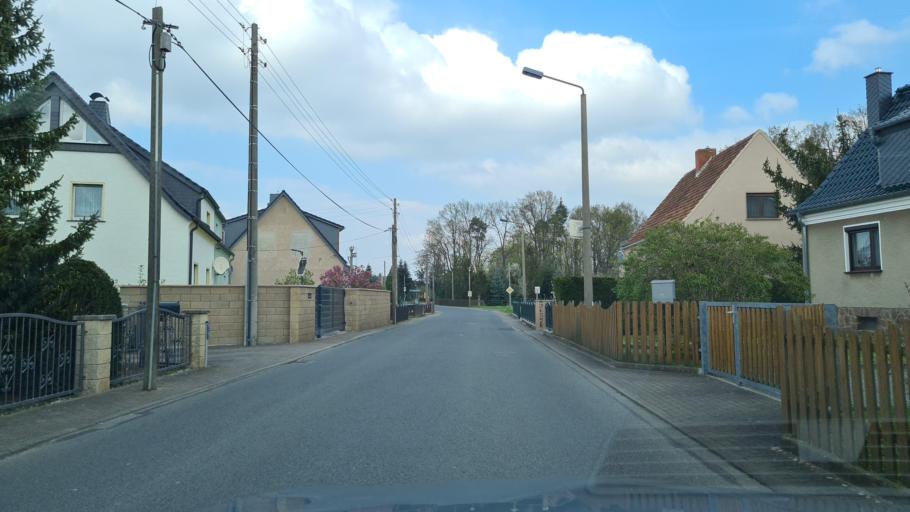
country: DE
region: Saxony
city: Wulknitz
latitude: 51.3737
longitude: 13.4229
